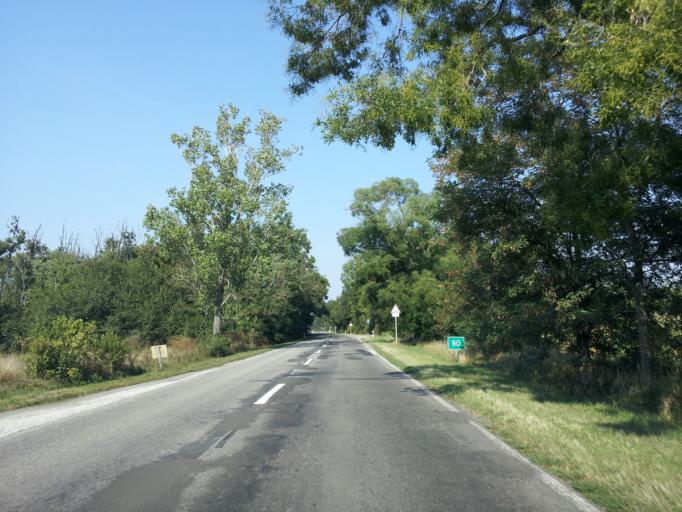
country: HU
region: Fejer
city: Polgardi
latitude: 47.0213
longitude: 18.2809
